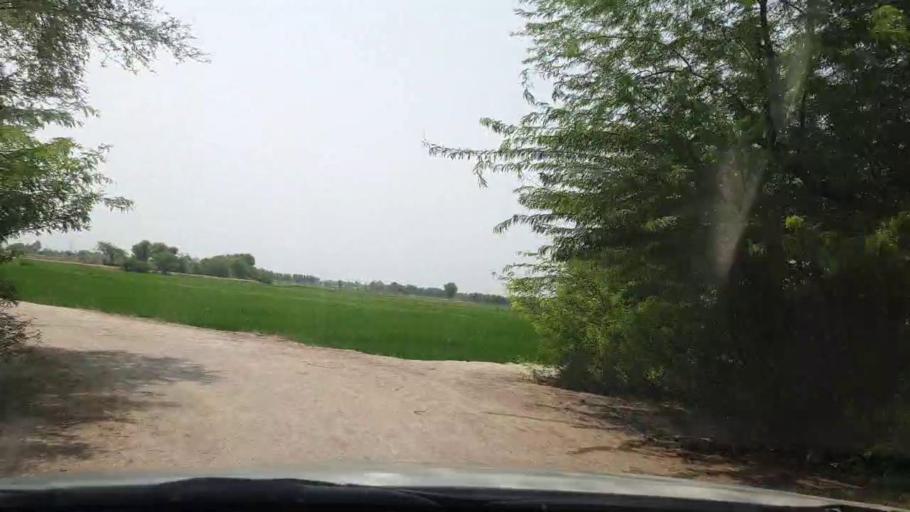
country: PK
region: Sindh
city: Shikarpur
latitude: 27.9849
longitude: 68.7165
